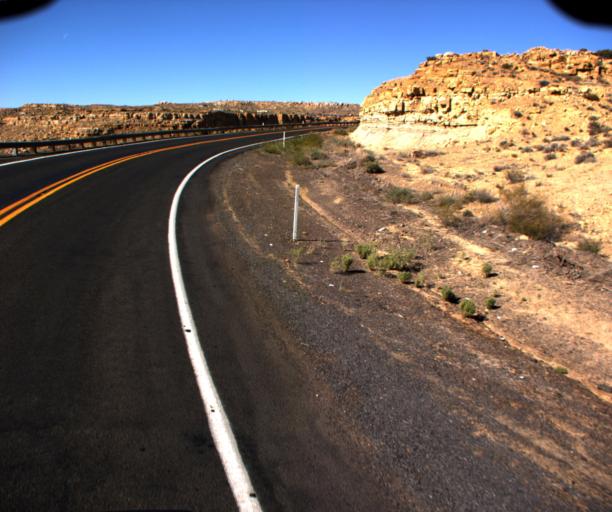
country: US
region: Arizona
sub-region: Navajo County
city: First Mesa
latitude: 35.8802
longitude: -110.6252
